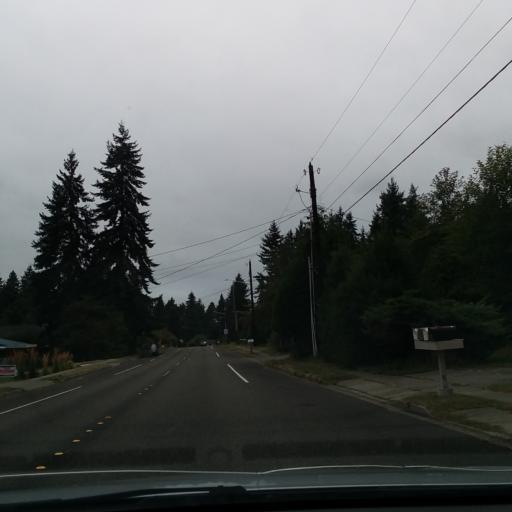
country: US
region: Washington
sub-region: Snohomish County
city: Lynnwood
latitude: 47.8229
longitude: -122.2997
